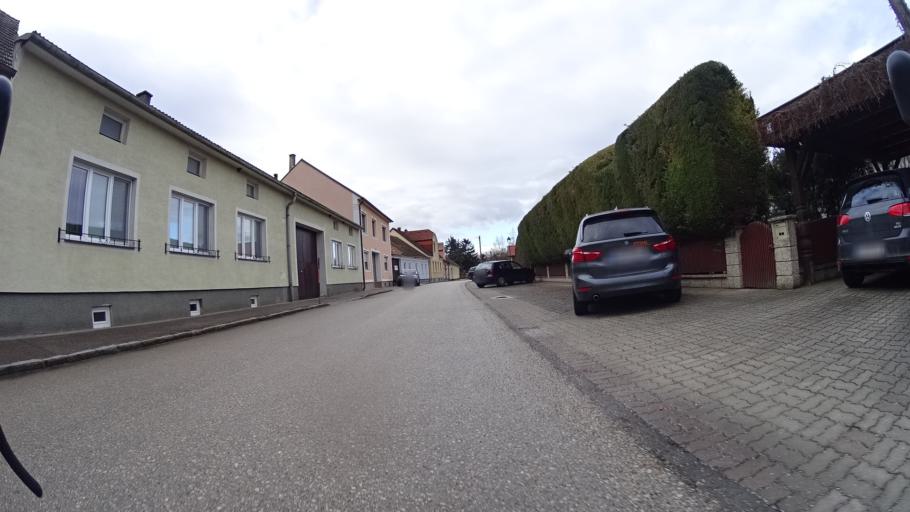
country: AT
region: Lower Austria
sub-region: Politischer Bezirk Tulln
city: Langenrohr
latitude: 48.3304
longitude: 15.9778
